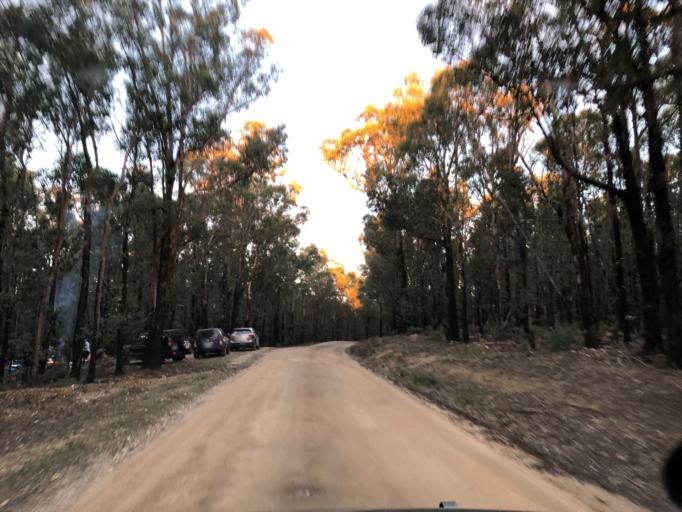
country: AU
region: Victoria
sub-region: Moorabool
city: Bacchus Marsh
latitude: -37.4755
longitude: 144.4250
